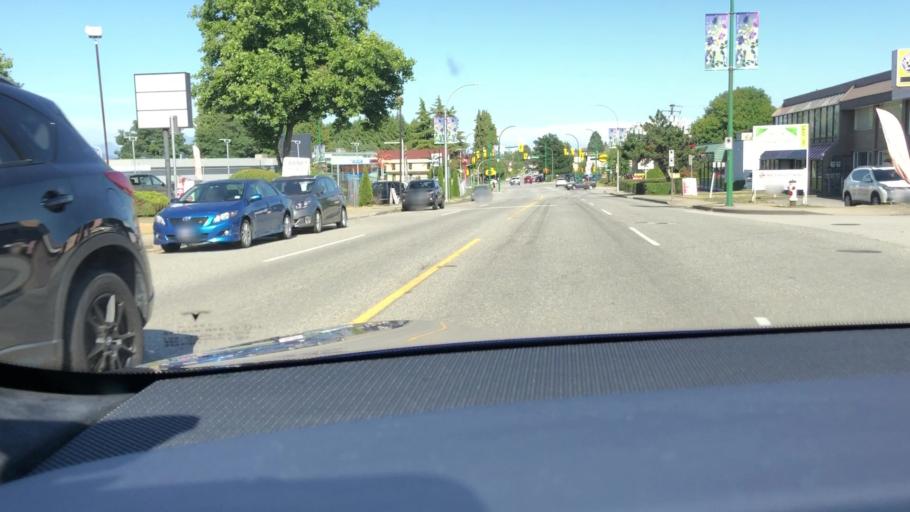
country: CA
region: British Columbia
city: Burnaby
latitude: 49.2219
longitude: -122.9819
